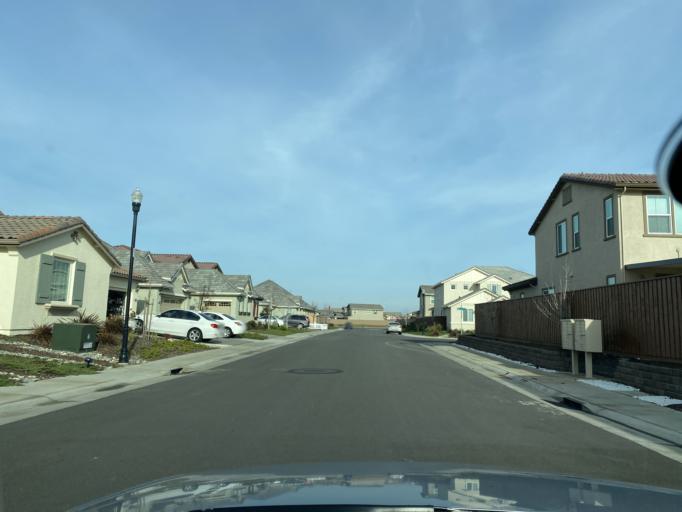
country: US
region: California
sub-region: Sacramento County
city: Elk Grove
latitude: 38.3914
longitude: -121.3956
